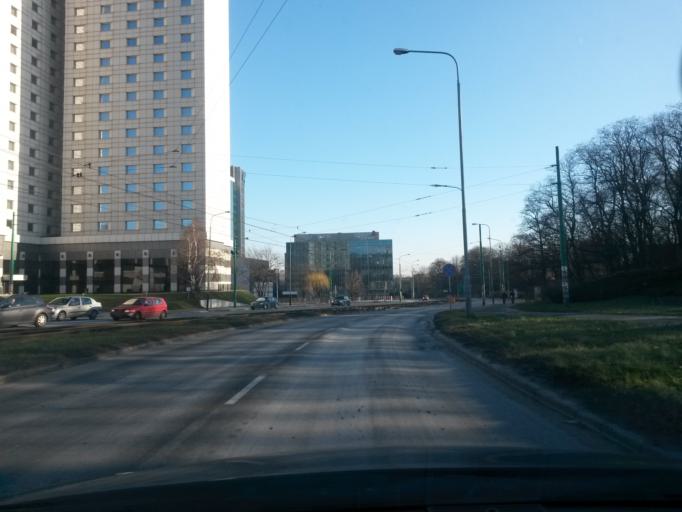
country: PL
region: Greater Poland Voivodeship
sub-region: Poznan
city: Poznan
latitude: 52.4014
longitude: 16.9224
